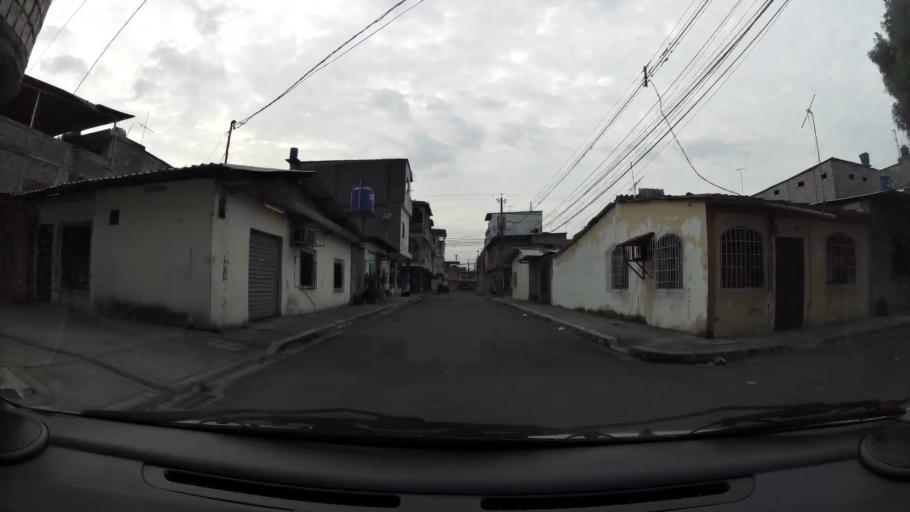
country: EC
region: Guayas
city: Guayaquil
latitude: -2.2441
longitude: -79.8919
